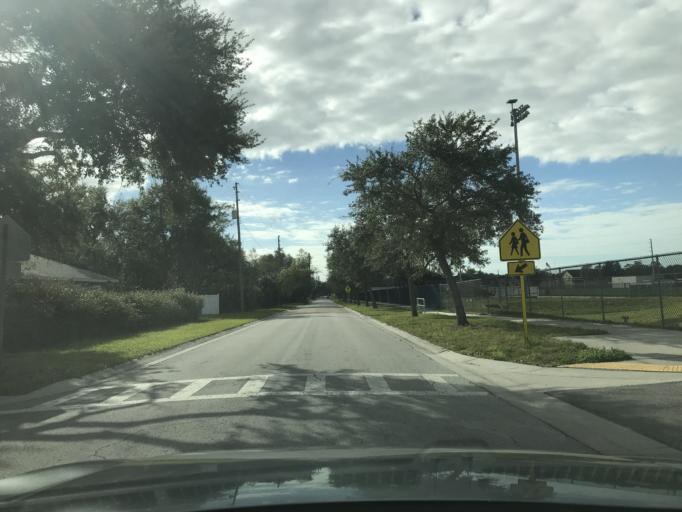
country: US
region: Florida
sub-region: Pinellas County
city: Largo
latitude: 27.9204
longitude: -82.7834
